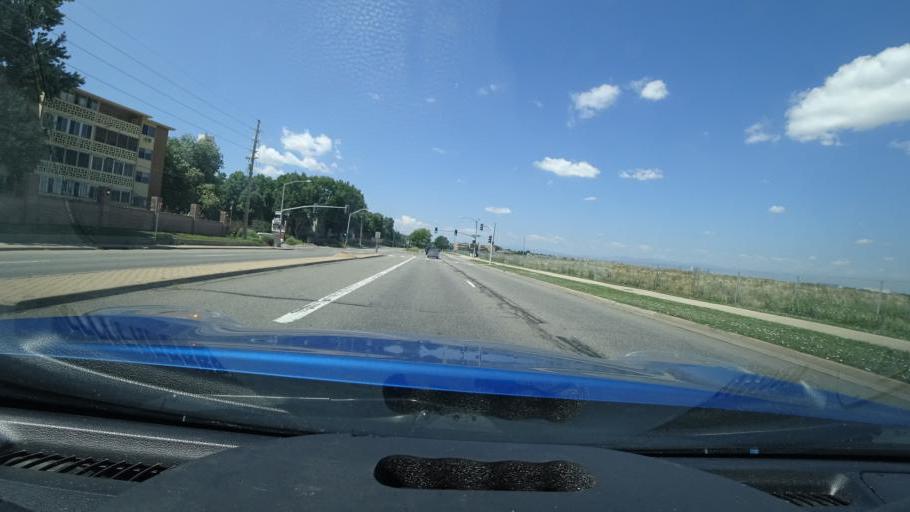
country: US
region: Colorado
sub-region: Adams County
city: Aurora
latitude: 39.7084
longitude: -104.8782
